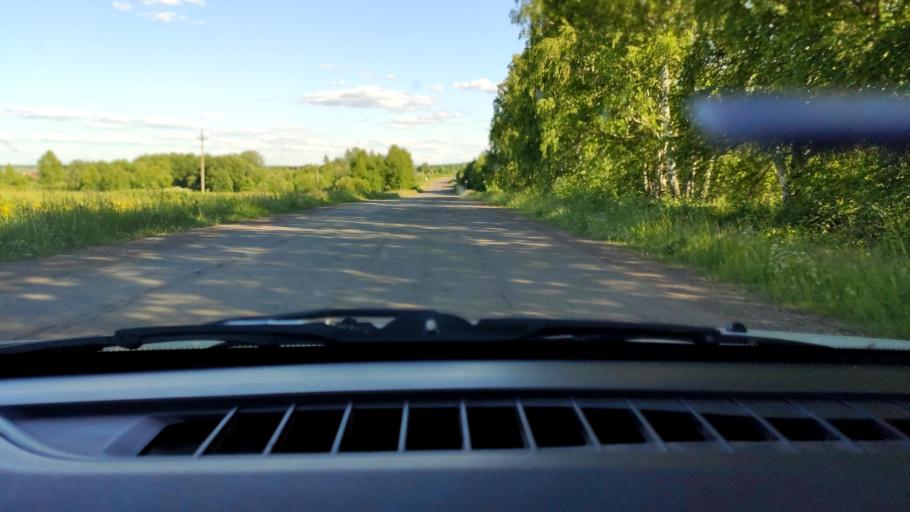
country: RU
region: Perm
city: Uinskoye
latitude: 57.0913
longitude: 56.5547
